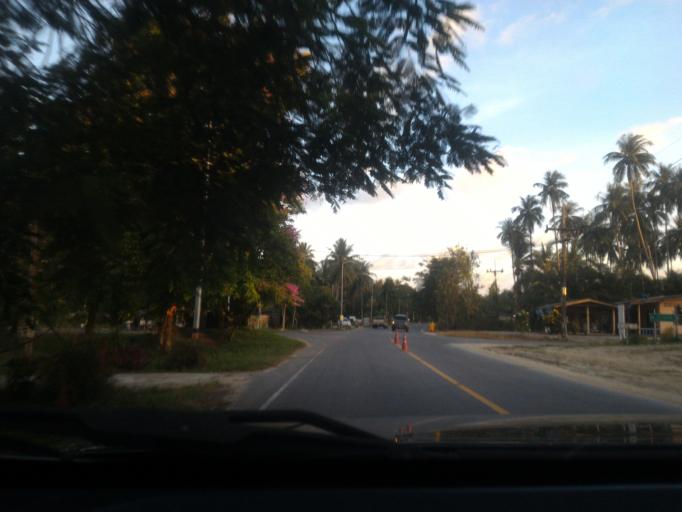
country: TH
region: Surat Thani
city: Don Sak
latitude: 9.0450
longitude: 99.9027
